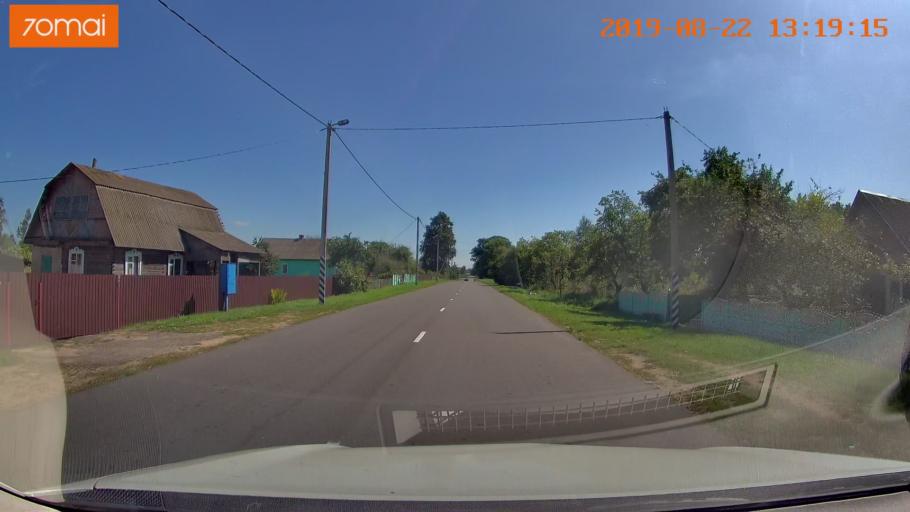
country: BY
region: Minsk
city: Urechcha
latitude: 53.2358
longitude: 27.9492
